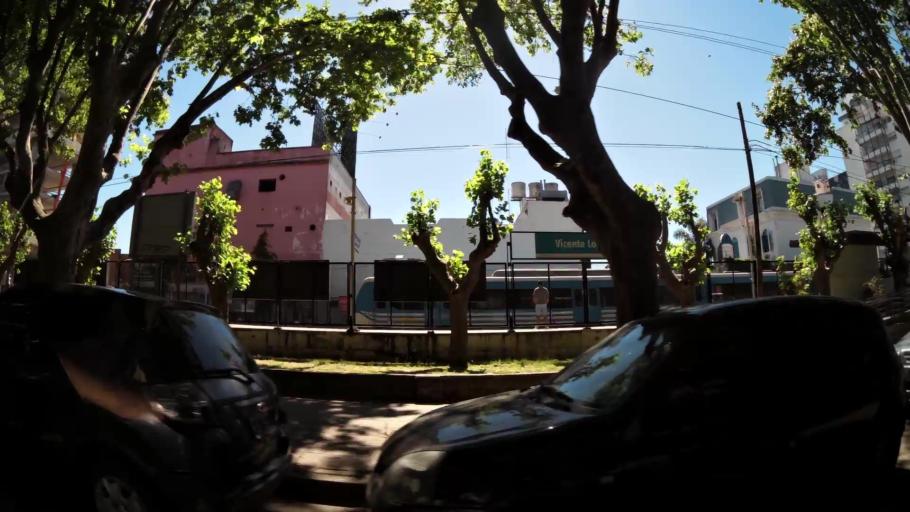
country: AR
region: Buenos Aires
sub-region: Partido de Vicente Lopez
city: Olivos
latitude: -34.5256
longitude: -58.4726
